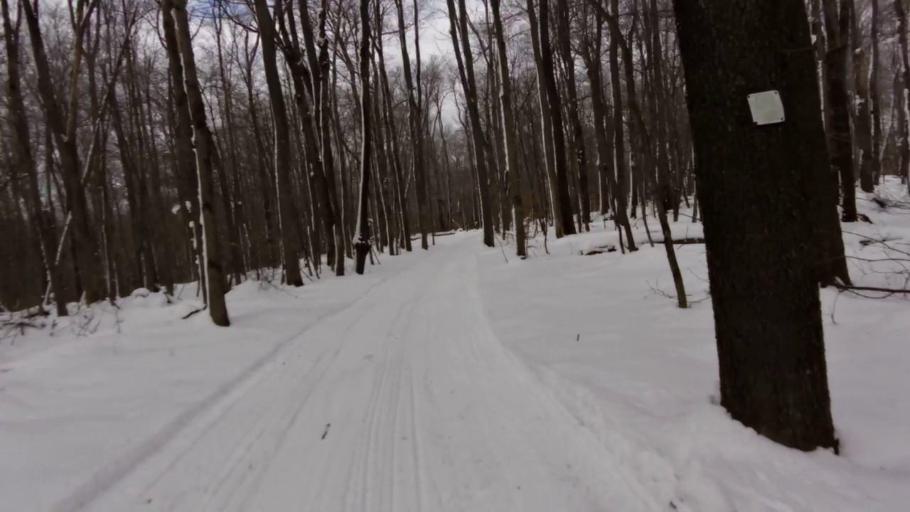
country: US
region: Pennsylvania
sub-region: McKean County
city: Bradford
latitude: 42.0262
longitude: -78.7409
